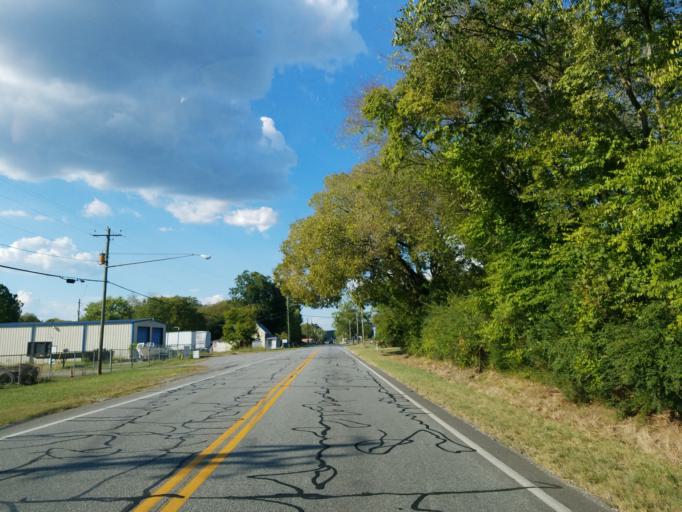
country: US
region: Georgia
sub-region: Bartow County
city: Rydal
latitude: 34.4976
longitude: -84.7095
